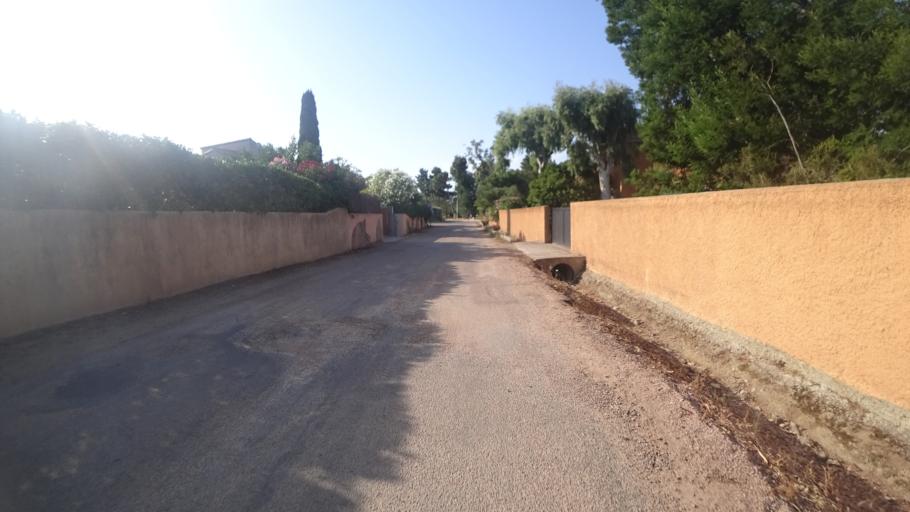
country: FR
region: Corsica
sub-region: Departement de la Corse-du-Sud
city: Porto-Vecchio
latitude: 41.6367
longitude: 9.3434
